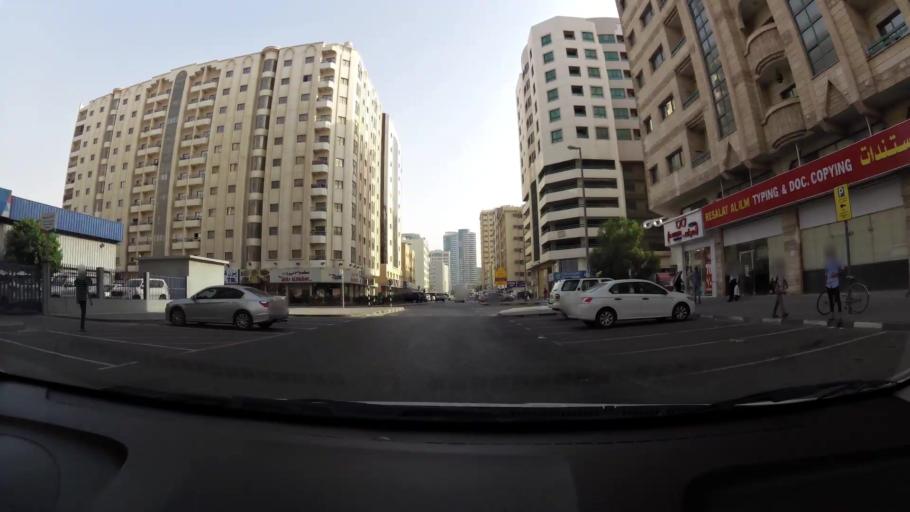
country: AE
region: Ash Shariqah
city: Sharjah
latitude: 25.3347
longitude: 55.3982
